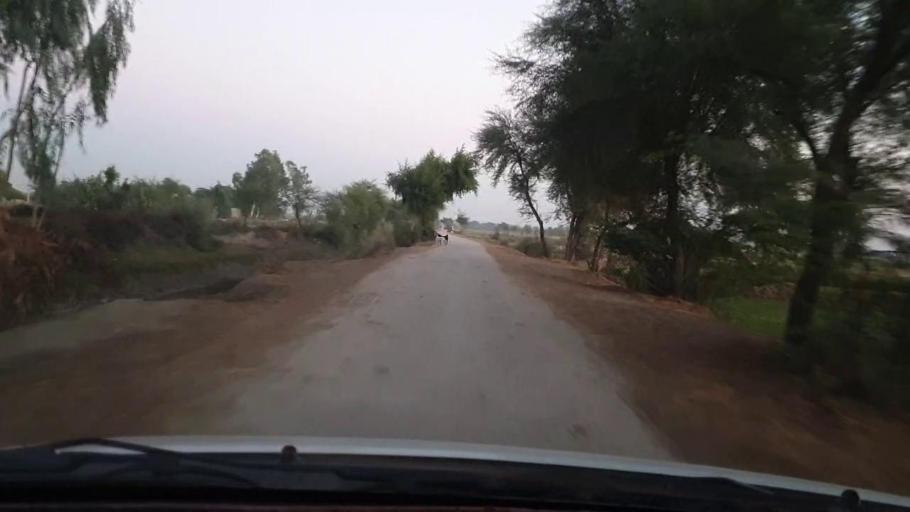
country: PK
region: Sindh
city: Khairpur Nathan Shah
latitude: 27.1448
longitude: 67.7078
